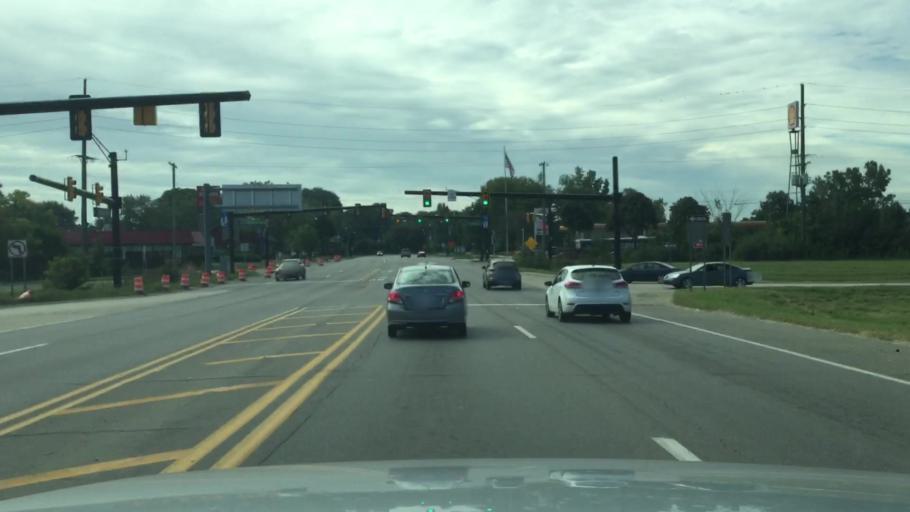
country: US
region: Michigan
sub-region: Wayne County
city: Belleville
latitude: 42.2186
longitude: -83.4853
